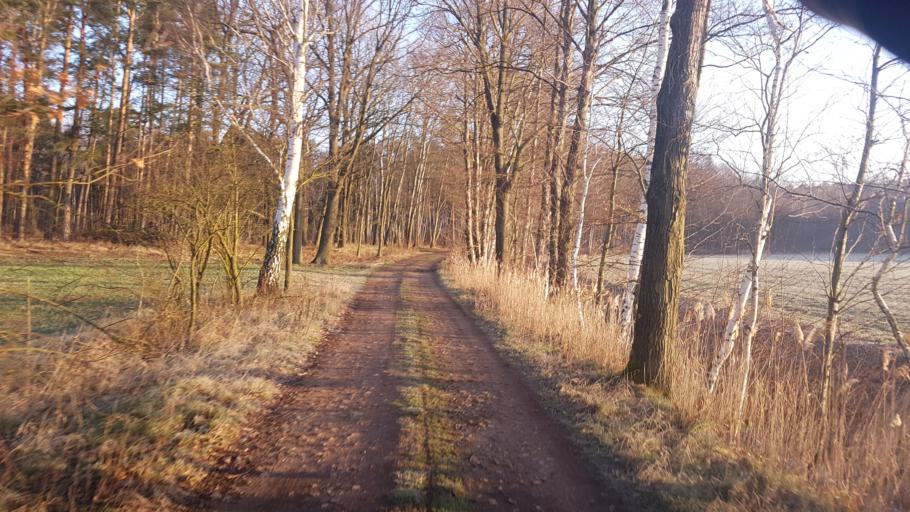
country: DE
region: Brandenburg
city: Finsterwalde
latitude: 51.6712
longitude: 13.7494
